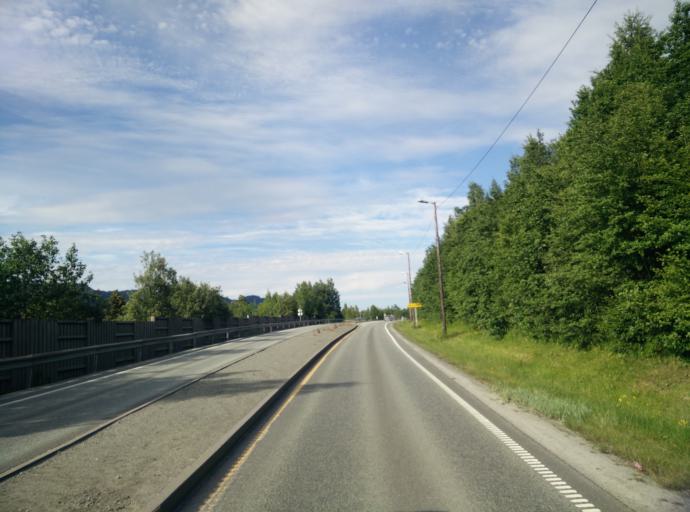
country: NO
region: Sor-Trondelag
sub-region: Orkdal
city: Orkanger
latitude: 63.3064
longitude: 9.8546
